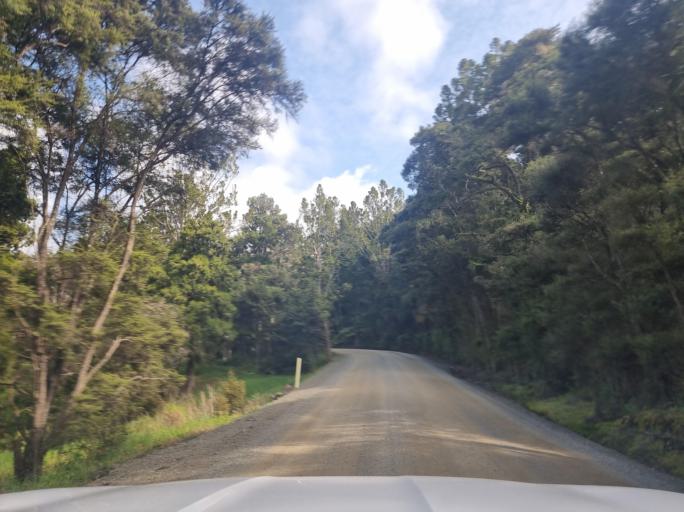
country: NZ
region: Auckland
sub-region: Auckland
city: Wellsford
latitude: -36.1007
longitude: 174.5054
